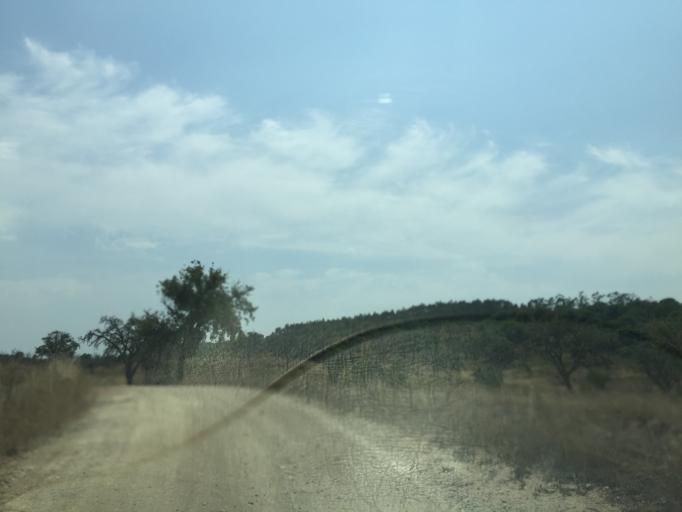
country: PT
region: Setubal
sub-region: Grandola
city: Grandola
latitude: 38.1052
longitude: -8.4889
